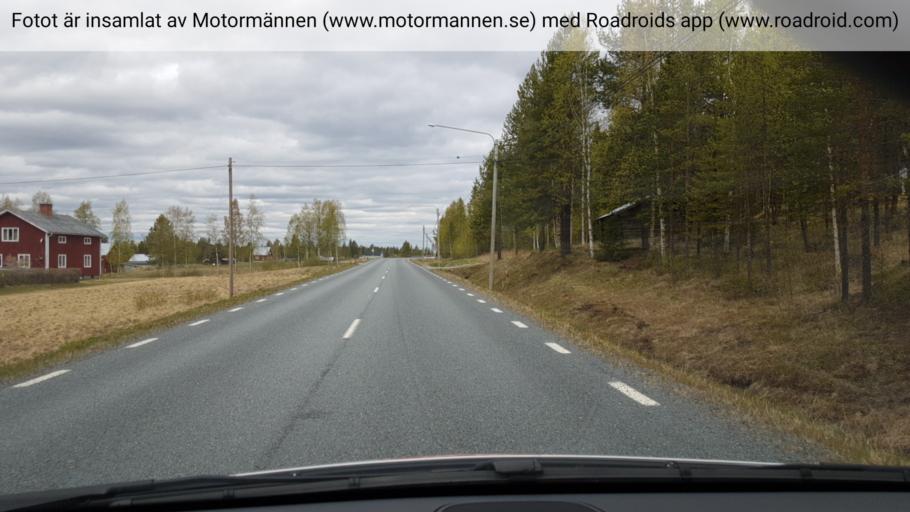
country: SE
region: Vaesterbotten
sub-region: Lycksele Kommun
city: Soderfors
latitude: 65.1126
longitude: 18.2997
